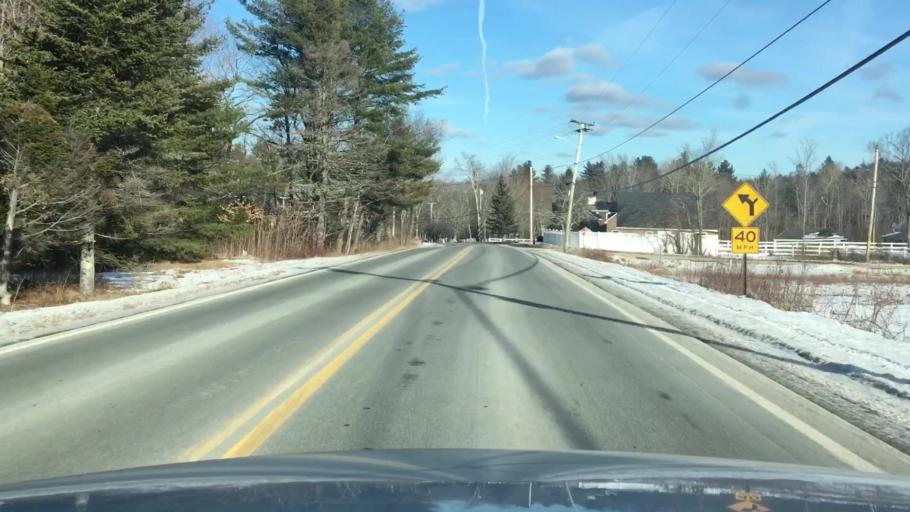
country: US
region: Maine
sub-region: Penobscot County
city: Holden
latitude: 44.7743
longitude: -68.5858
